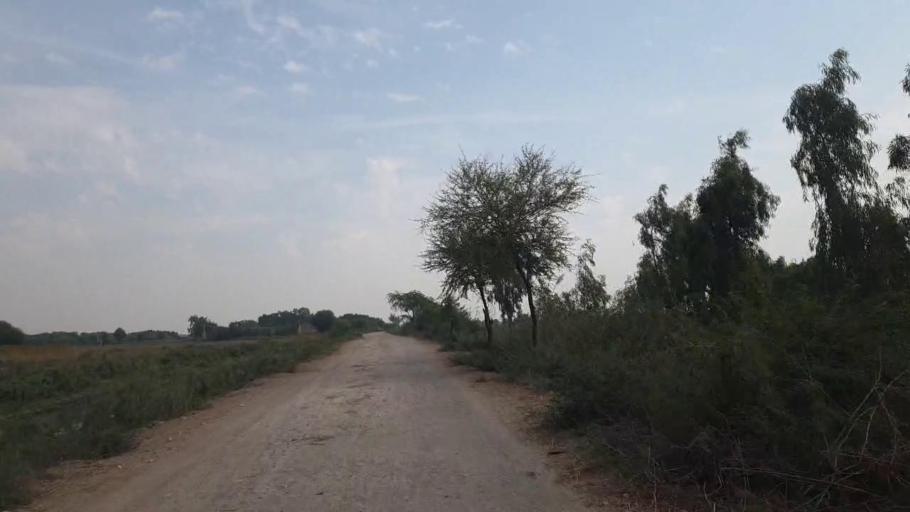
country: PK
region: Sindh
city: Rajo Khanani
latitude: 24.9587
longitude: 69.0045
